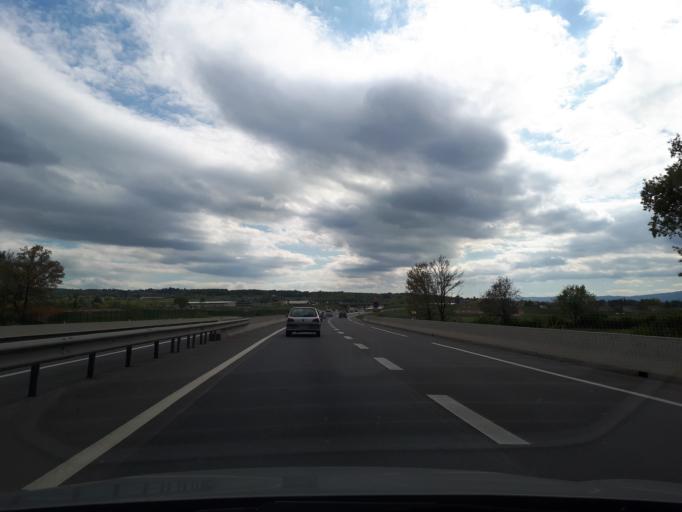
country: FR
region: Rhone-Alpes
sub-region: Departement de la Loire
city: La Fouillouse
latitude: 45.5295
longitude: 4.3026
